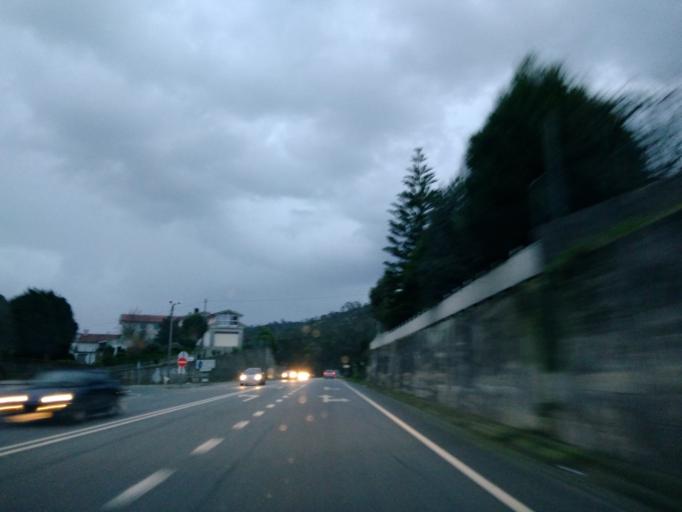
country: PT
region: Braga
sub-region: Braga
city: Oliveira
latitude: 41.4924
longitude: -8.4666
